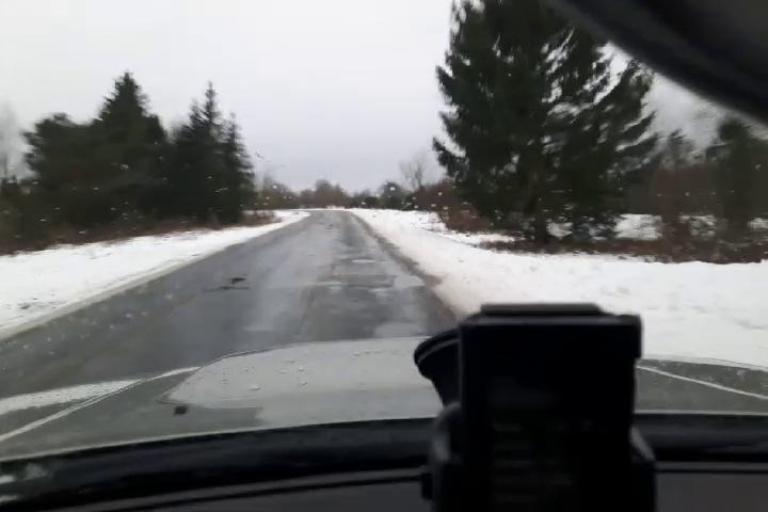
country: EE
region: Harju
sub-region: Harku vald
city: Tabasalu
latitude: 59.4252
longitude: 24.4251
